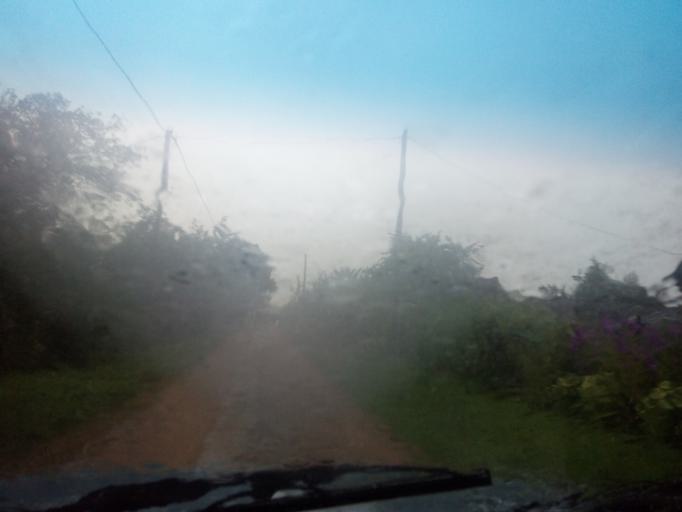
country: BY
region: Vitebsk
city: Dzisna
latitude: 55.6750
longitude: 28.3268
